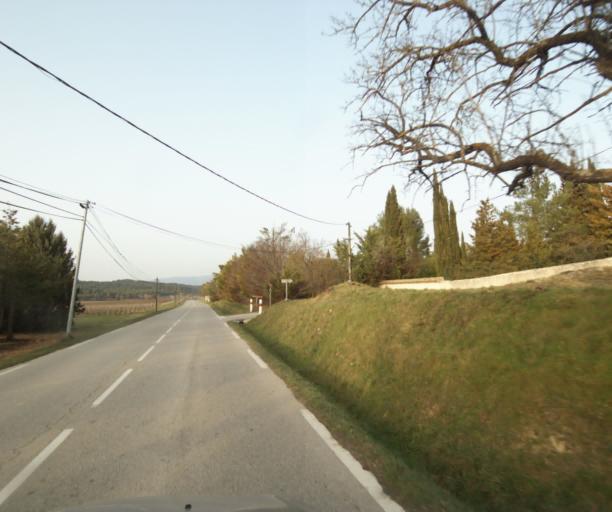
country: FR
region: Provence-Alpes-Cote d'Azur
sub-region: Departement des Bouches-du-Rhone
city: Rognes
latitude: 43.6921
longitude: 5.3432
